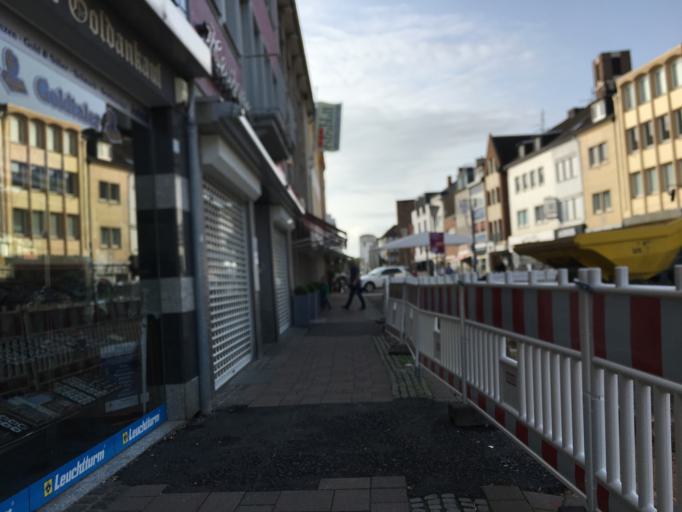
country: DE
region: North Rhine-Westphalia
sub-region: Regierungsbezirk Koln
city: Dueren
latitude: 50.8024
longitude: 6.4841
